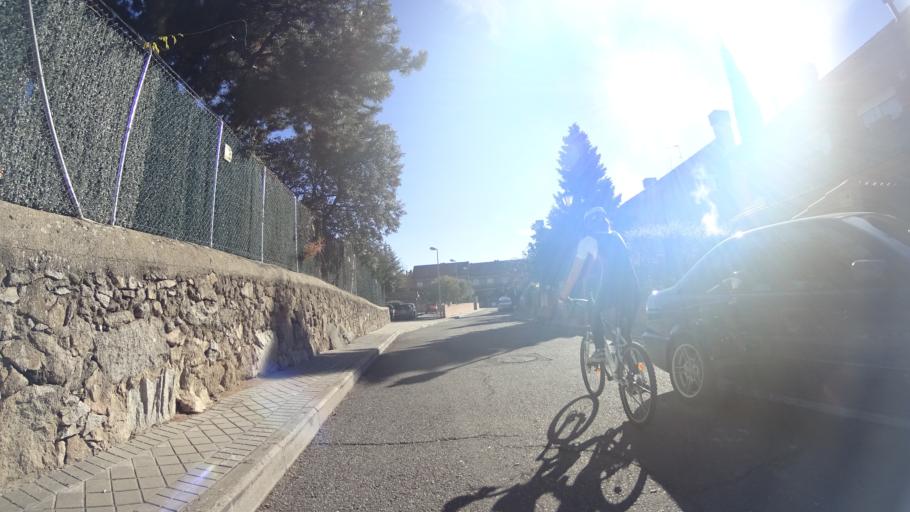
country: ES
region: Madrid
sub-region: Provincia de Madrid
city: Torrelodones
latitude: 40.5752
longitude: -3.9503
